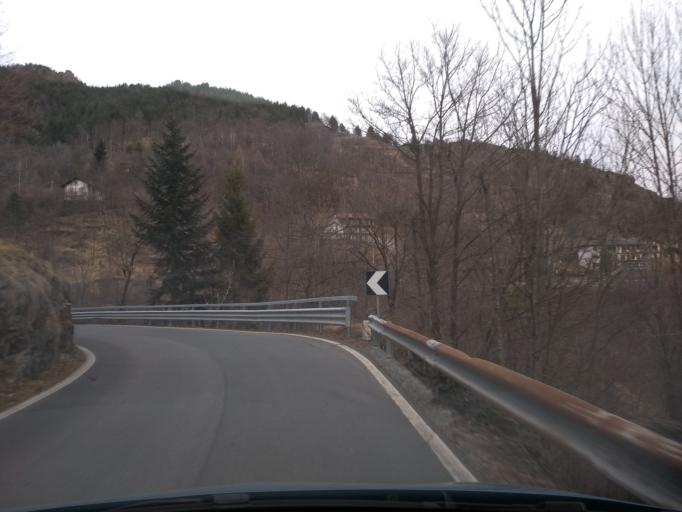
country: IT
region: Piedmont
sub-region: Provincia di Torino
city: Viu
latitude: 45.2375
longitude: 7.3902
